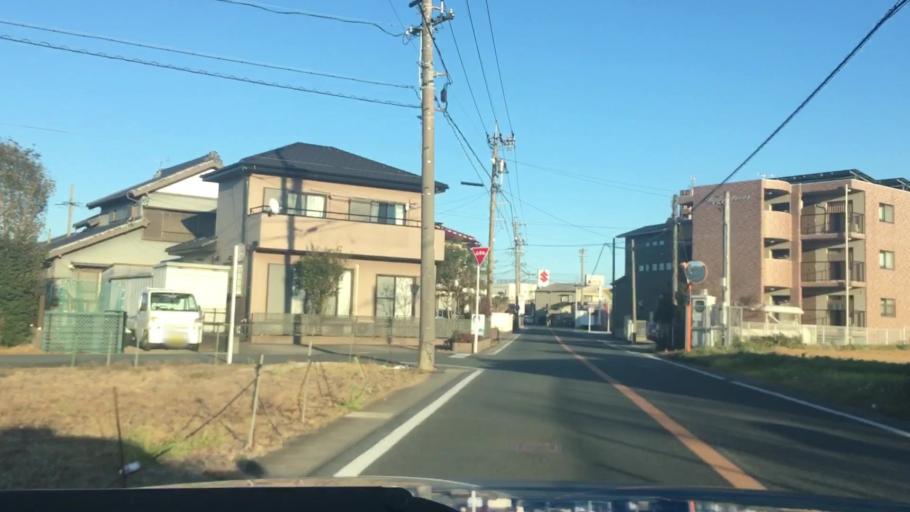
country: JP
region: Shizuoka
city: Hamamatsu
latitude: 34.7411
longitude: 137.6759
